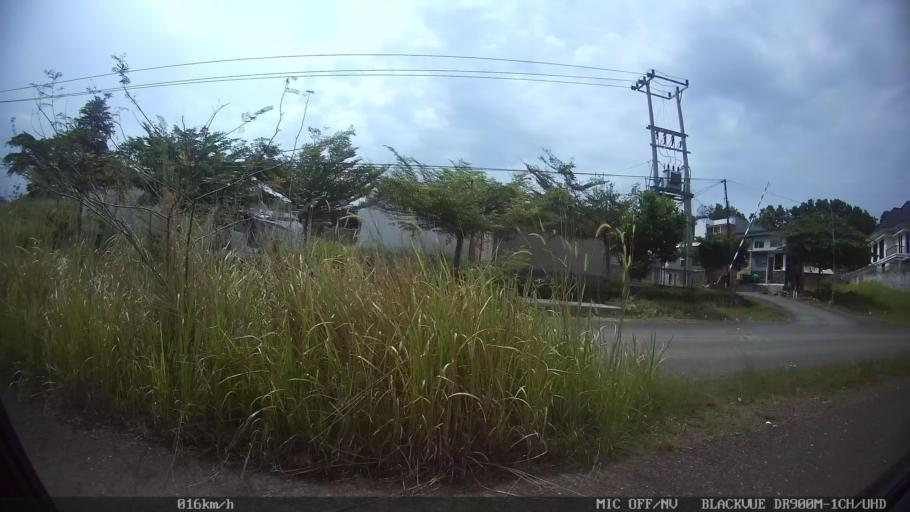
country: ID
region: Lampung
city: Bandarlampung
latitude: -5.4136
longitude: 105.1968
